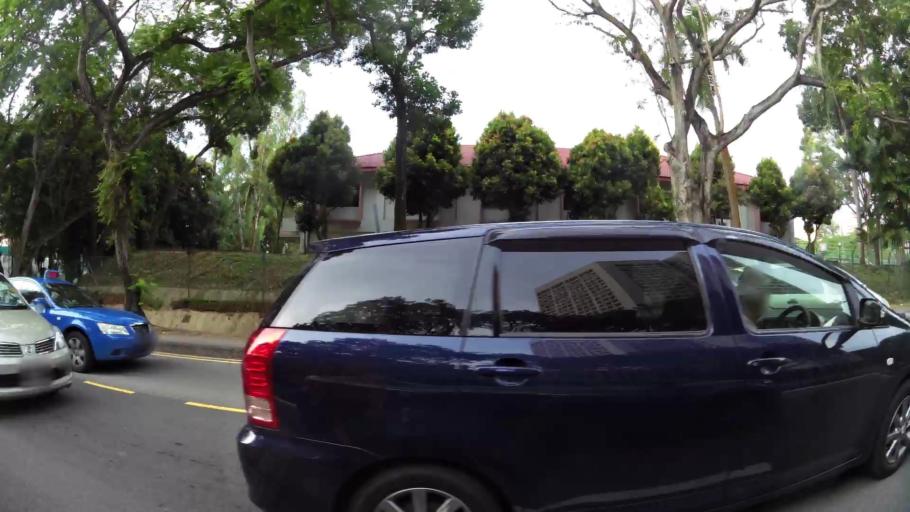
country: SG
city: Singapore
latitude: 1.2837
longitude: 103.8192
